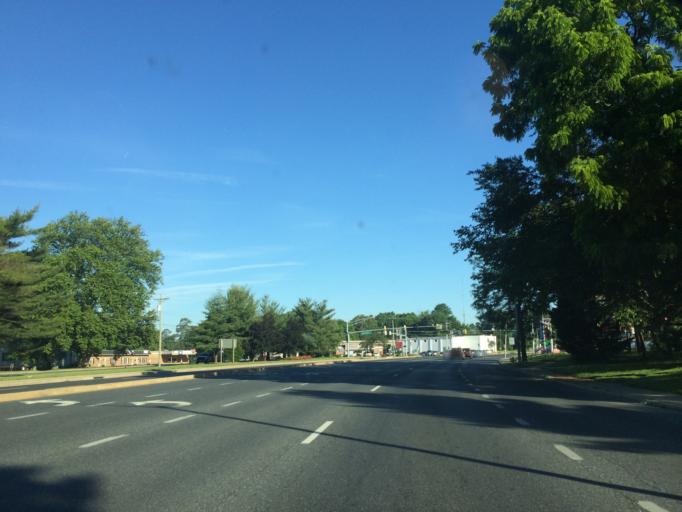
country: US
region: Maryland
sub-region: Wicomico County
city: Salisbury
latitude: 38.3688
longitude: -75.6129
